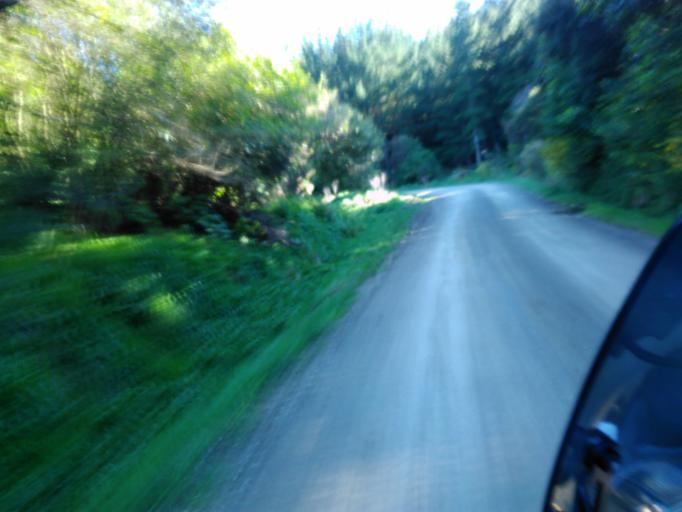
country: NZ
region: Gisborne
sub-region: Gisborne District
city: Gisborne
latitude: -38.3996
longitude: 177.6800
